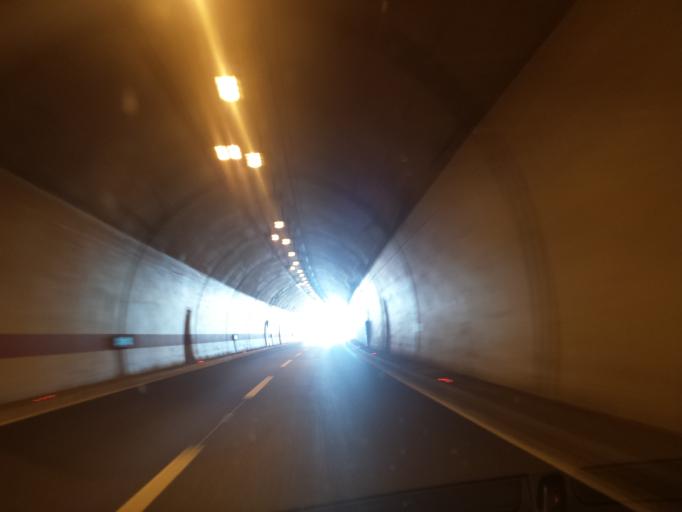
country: HR
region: Splitsko-Dalmatinska
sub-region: Grad Omis
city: Omis
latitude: 43.4790
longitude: 16.8230
